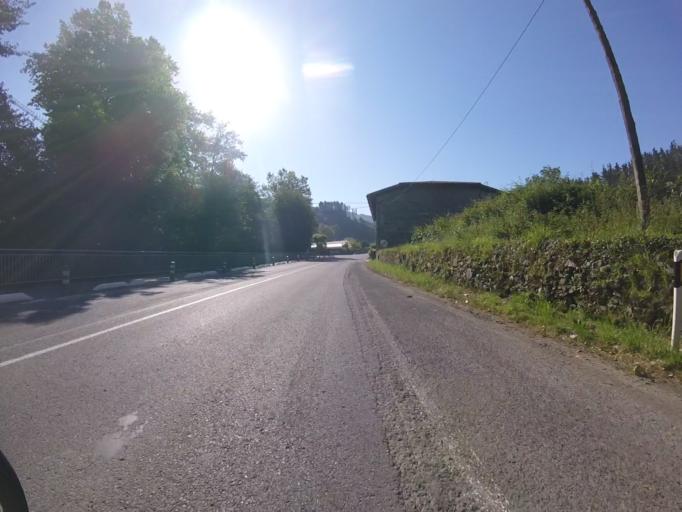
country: ES
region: Basque Country
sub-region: Provincia de Guipuzcoa
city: Azpeitia
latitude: 43.1701
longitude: -2.2535
